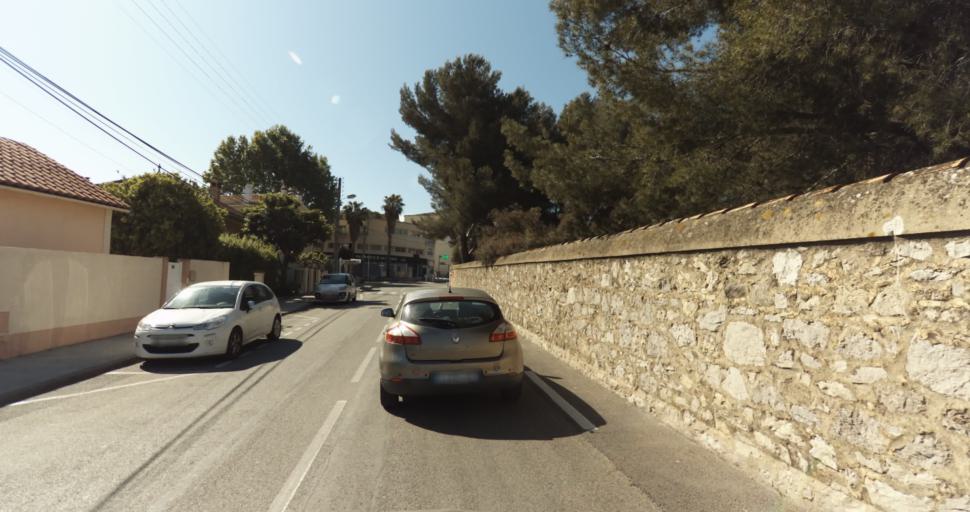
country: FR
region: Provence-Alpes-Cote d'Azur
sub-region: Departement du Var
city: La Seyne-sur-Mer
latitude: 43.0994
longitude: 5.8974
